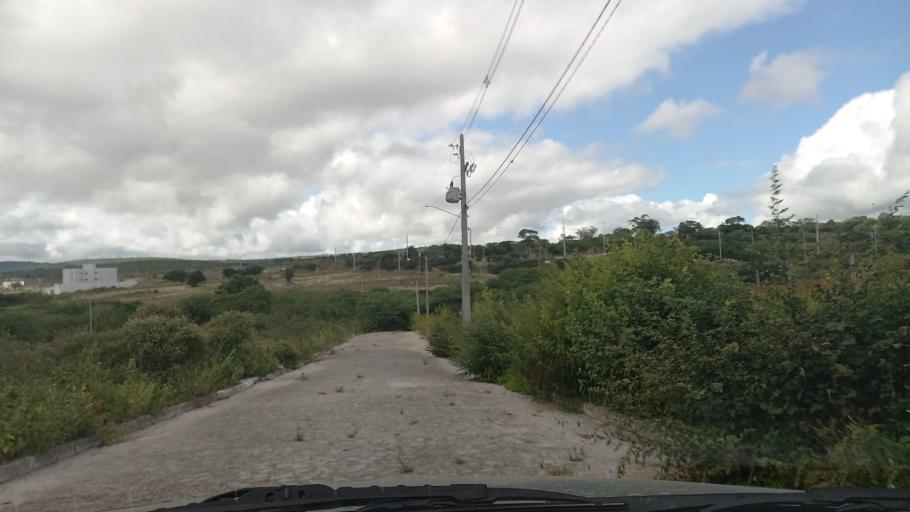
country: BR
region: Pernambuco
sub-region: Caruaru
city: Caruaru
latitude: -8.3048
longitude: -35.9606
